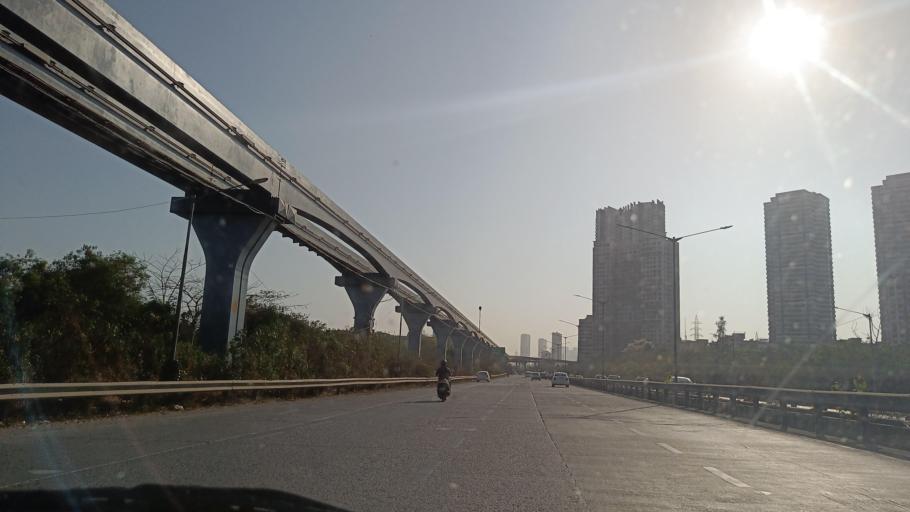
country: IN
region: Maharashtra
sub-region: Mumbai Suburban
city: Mumbai
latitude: 19.0268
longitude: 72.8835
